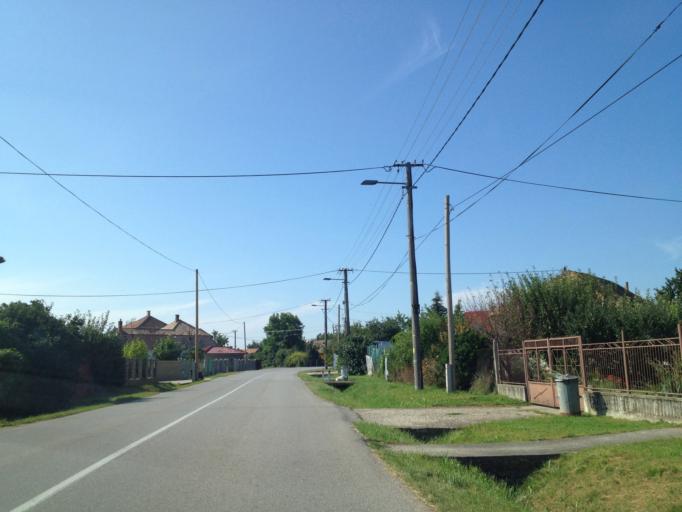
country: SK
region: Nitriansky
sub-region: Okres Komarno
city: Hurbanovo
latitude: 47.9023
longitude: 18.3072
